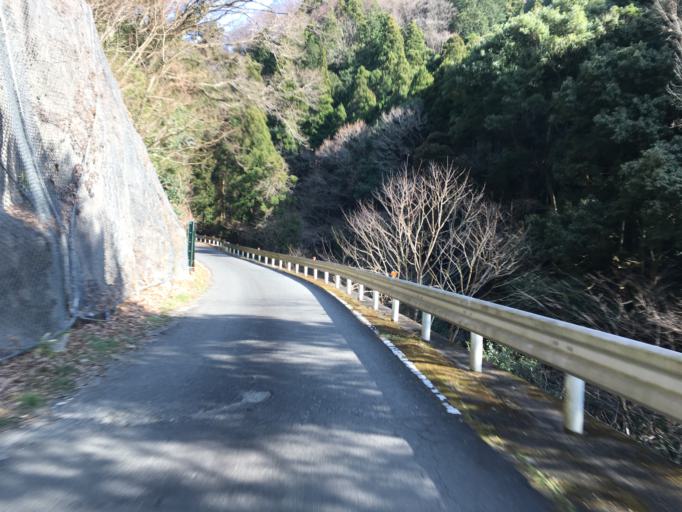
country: JP
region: Ibaraki
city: Kitaibaraki
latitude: 36.7766
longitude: 140.6856
